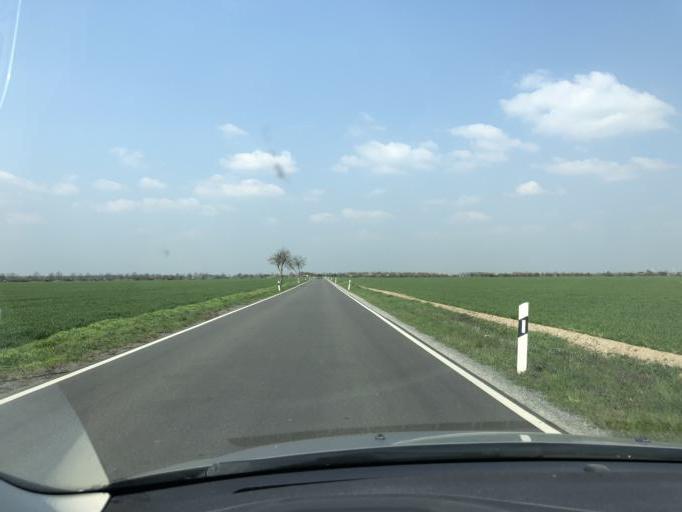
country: DE
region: Saxony
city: Wiedemar
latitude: 51.4824
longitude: 12.2240
